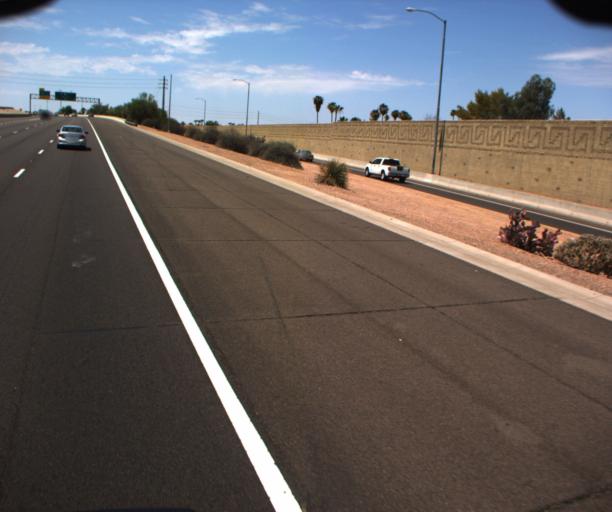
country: US
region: Arizona
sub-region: Maricopa County
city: Guadalupe
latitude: 33.3864
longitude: -111.9570
